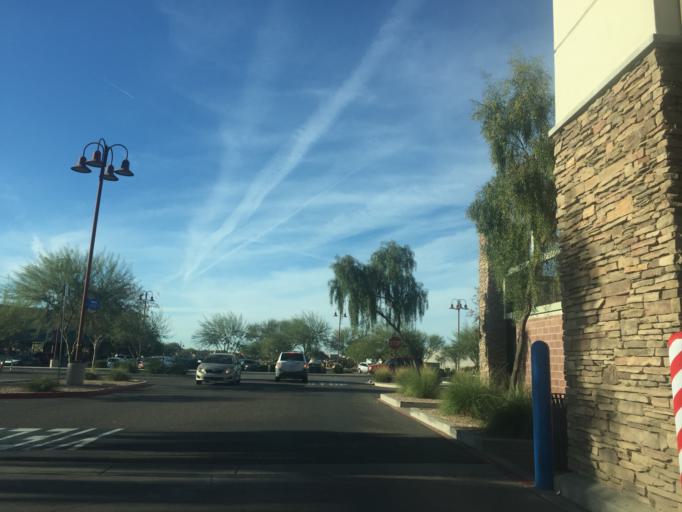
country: US
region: Arizona
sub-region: Maricopa County
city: Queen Creek
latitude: 33.2514
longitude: -111.6307
